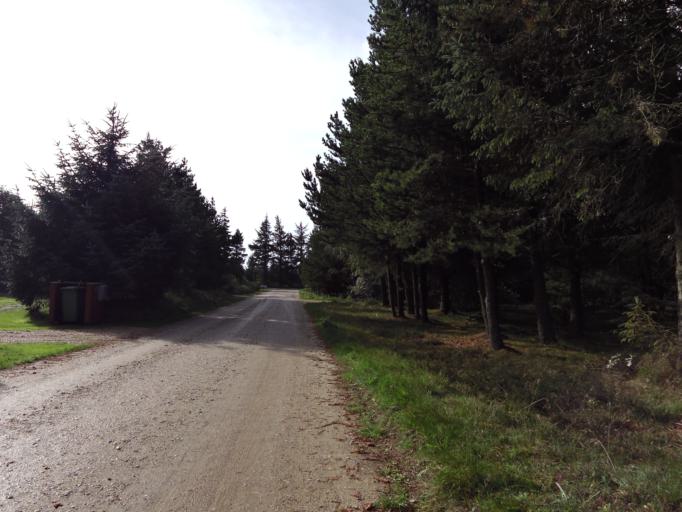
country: DK
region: South Denmark
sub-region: Varde Kommune
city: Oksbol
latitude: 55.5511
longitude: 8.2109
